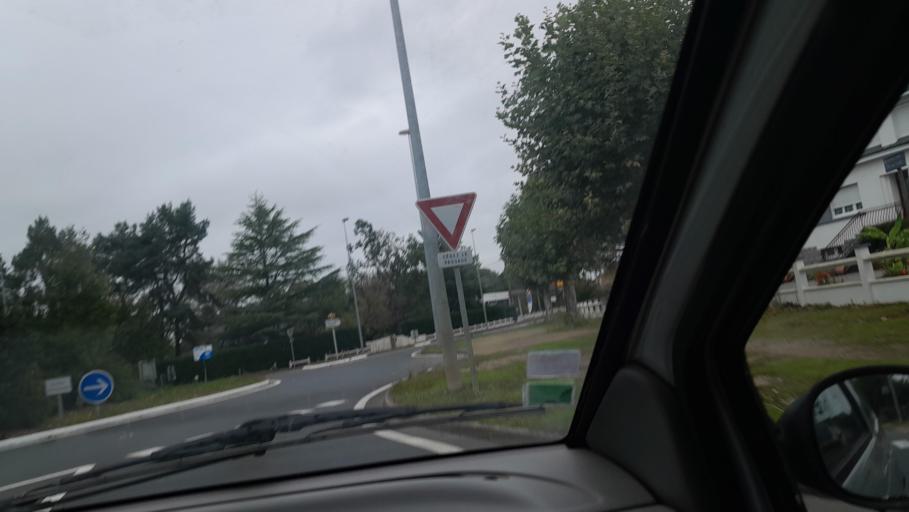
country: FR
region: Pays de la Loire
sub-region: Departement de la Loire-Atlantique
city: Saint-Mars-la-Jaille
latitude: 47.5246
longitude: -1.1755
